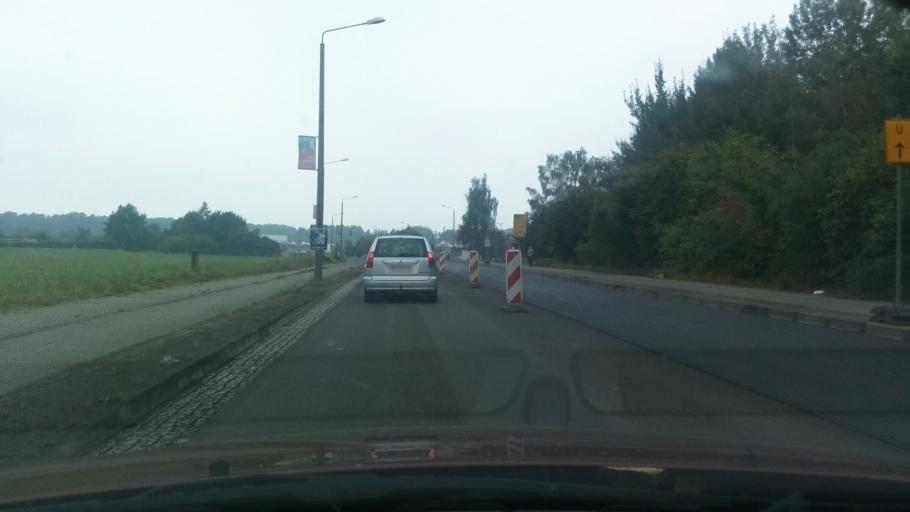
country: DE
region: Saxony
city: Goerlitz
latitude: 51.1657
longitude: 14.9712
